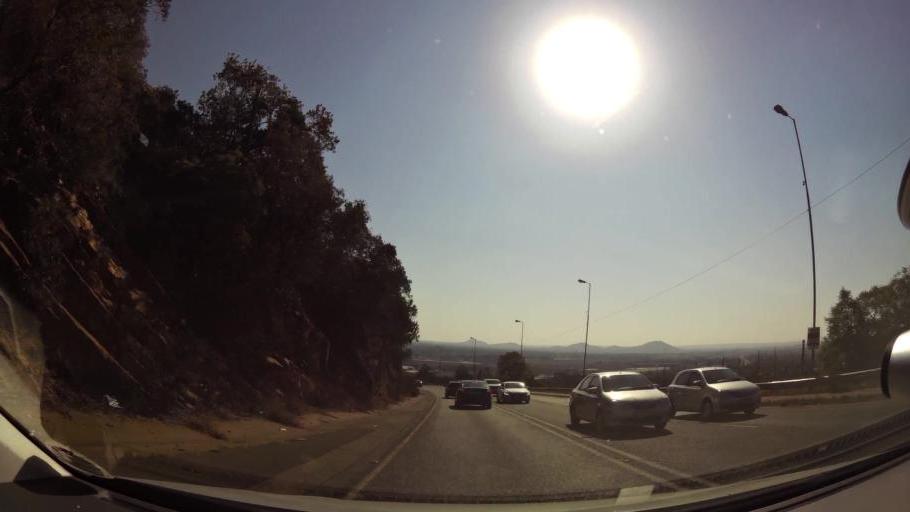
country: ZA
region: Gauteng
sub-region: City of Tshwane Metropolitan Municipality
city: Pretoria
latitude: -25.6898
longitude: 28.1974
